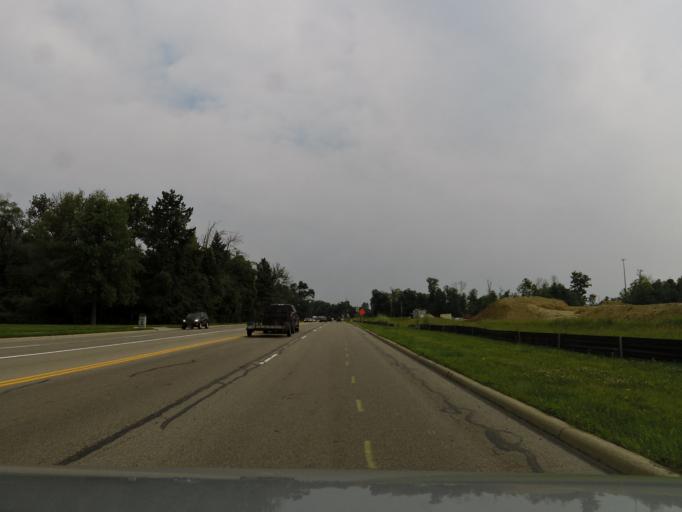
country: US
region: Ohio
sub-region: Greene County
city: Bellbrook
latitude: 39.6633
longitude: -84.1090
